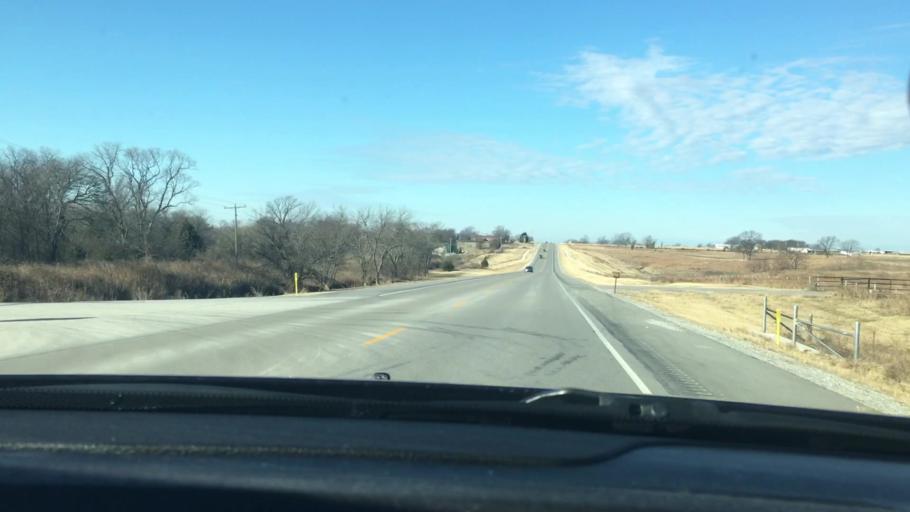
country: US
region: Oklahoma
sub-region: Love County
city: Marietta
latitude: 33.9404
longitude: -97.1779
